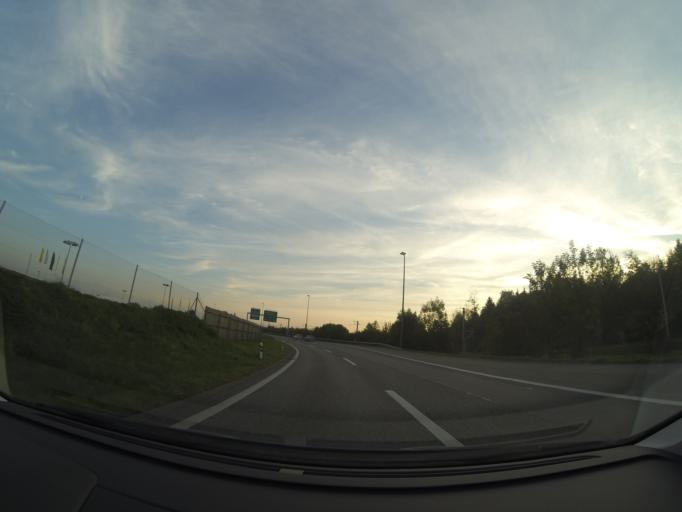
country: CH
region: Zurich
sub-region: Bezirk Hinwil
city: Bubikon
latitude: 47.2902
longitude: 8.8156
